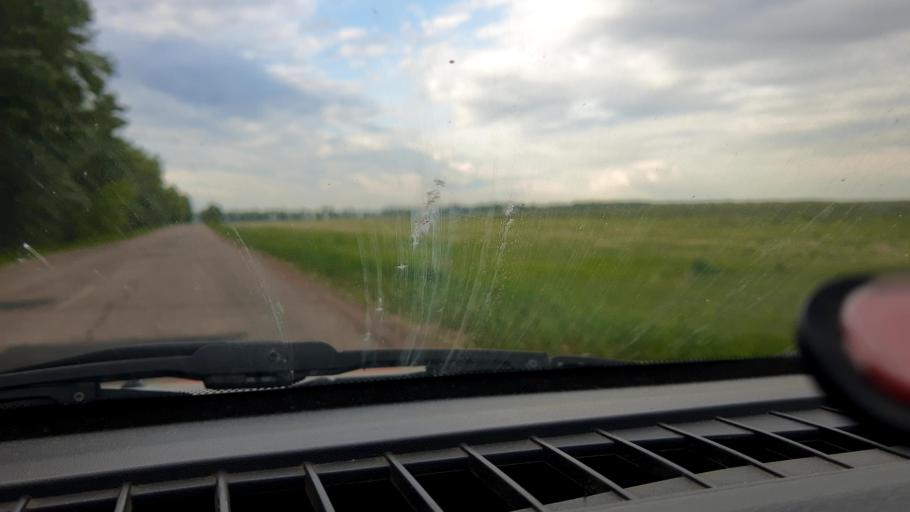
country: RU
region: Bashkortostan
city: Asanovo
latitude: 54.8227
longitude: 55.5957
